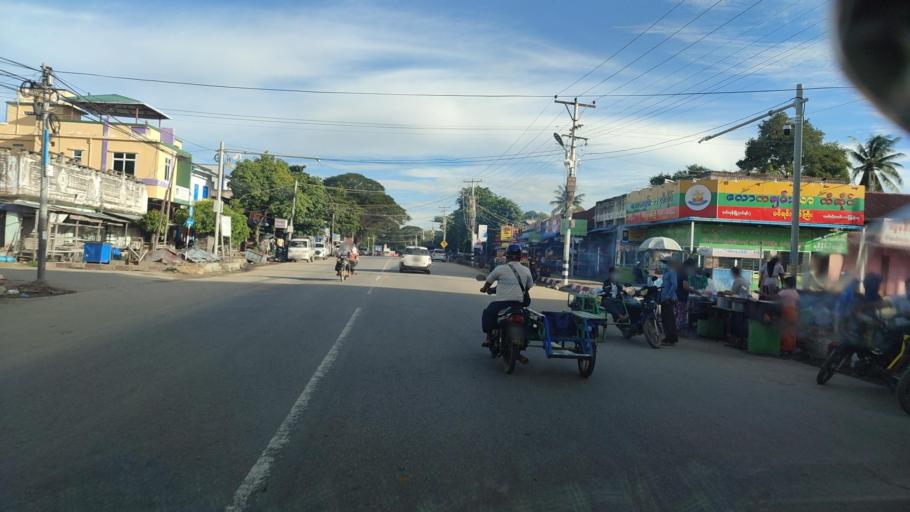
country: MM
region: Mandalay
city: Yamethin
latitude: 20.1316
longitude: 96.2010
